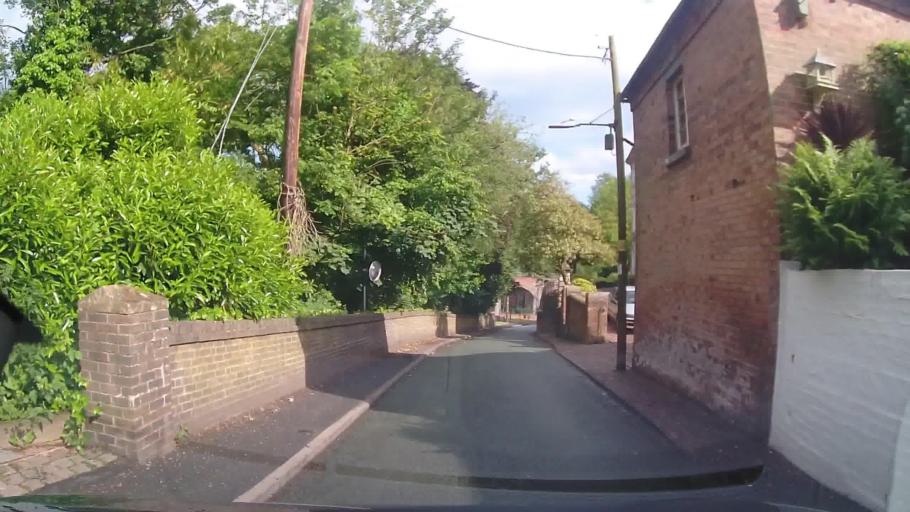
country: GB
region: England
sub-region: Telford and Wrekin
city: Ironbridge
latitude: 52.6416
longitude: -2.4941
